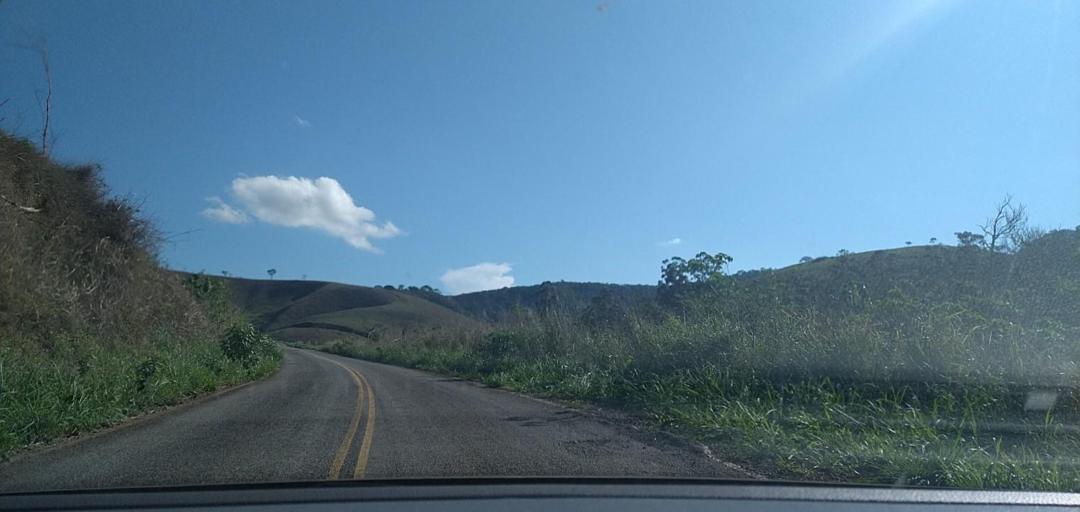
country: BR
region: Minas Gerais
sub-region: Alvinopolis
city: Alvinopolis
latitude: -20.1872
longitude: -42.9376
